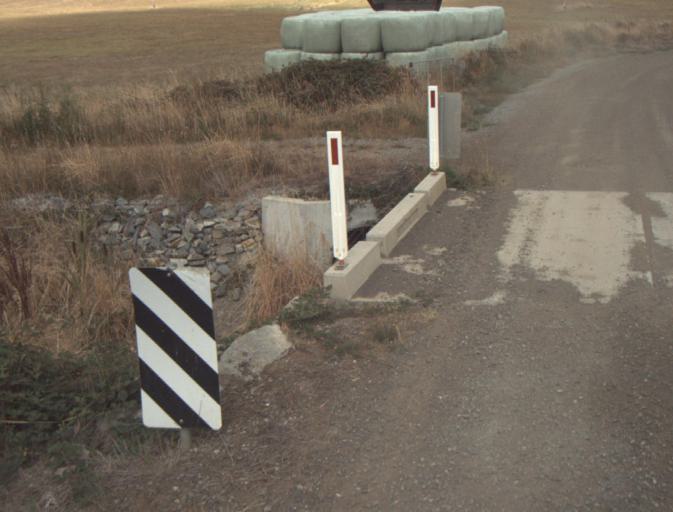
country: AU
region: Tasmania
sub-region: Launceston
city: Mayfield
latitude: -41.2132
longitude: 147.1482
